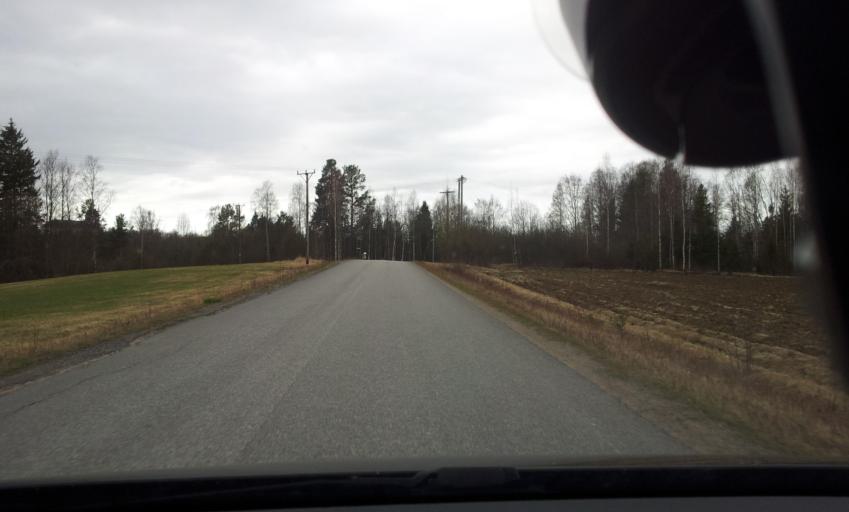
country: SE
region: Gaevleborg
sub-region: Ljusdals Kommun
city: Farila
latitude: 61.8069
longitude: 15.8584
